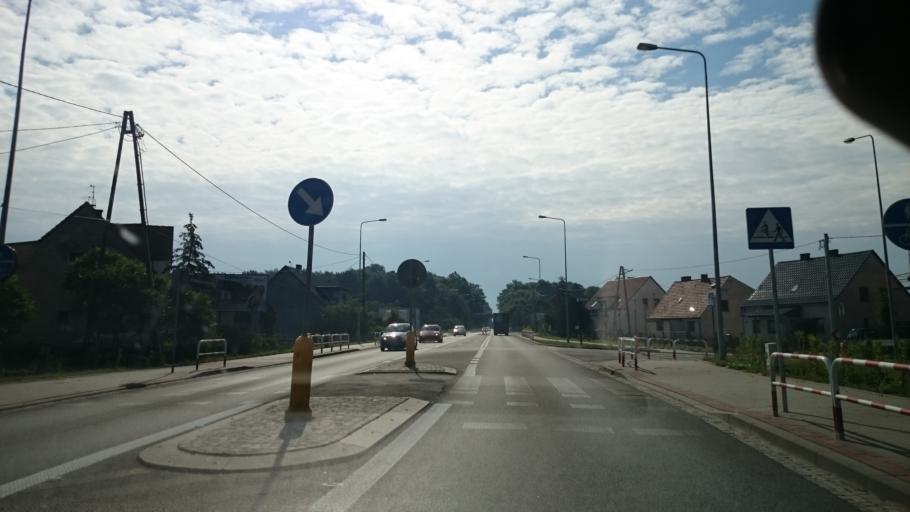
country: PL
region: Opole Voivodeship
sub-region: Powiat strzelecki
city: Strzelce Opolskie
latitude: 50.5040
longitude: 18.3282
